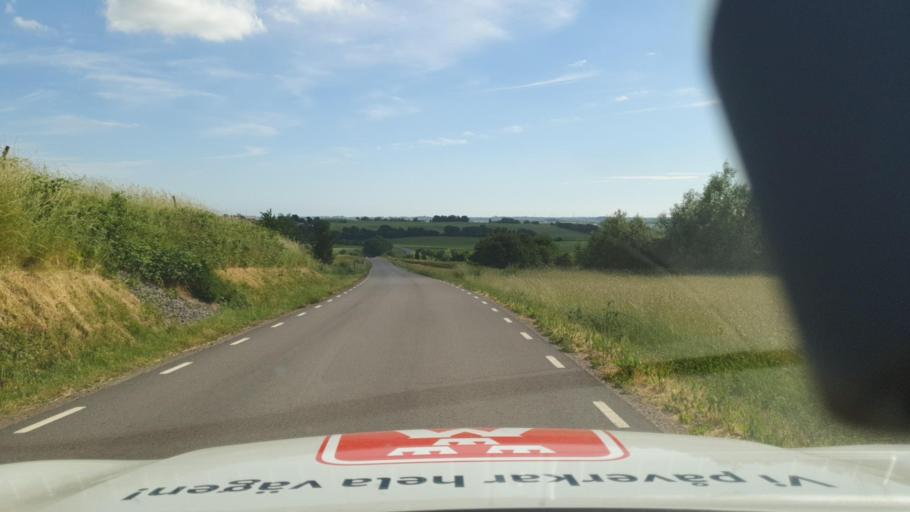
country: SE
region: Skane
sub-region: Sjobo Kommun
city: Blentarp
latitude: 55.5355
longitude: 13.5492
